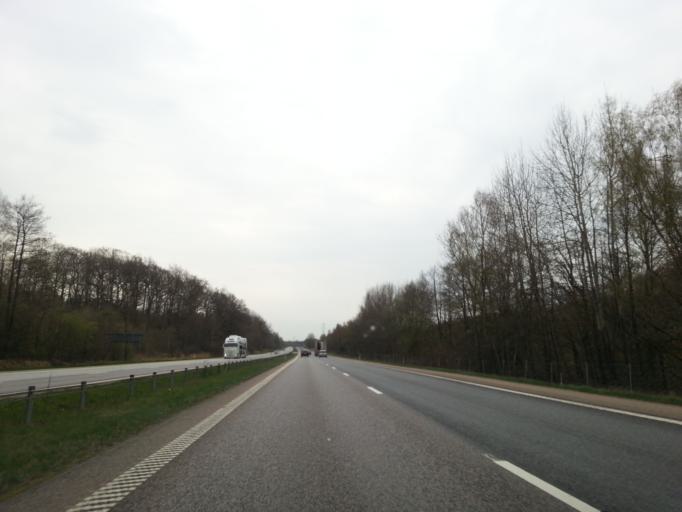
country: SE
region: Halland
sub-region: Halmstads Kommun
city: Halmstad
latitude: 56.7061
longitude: 12.8902
